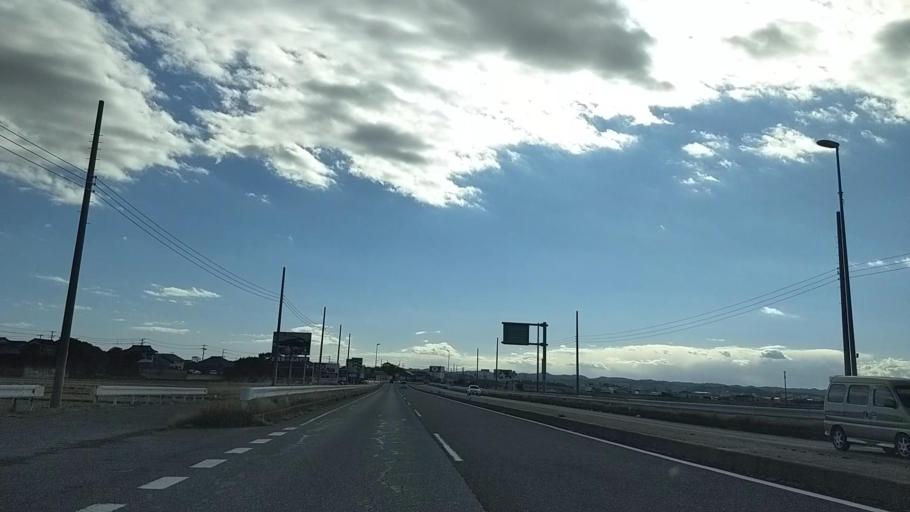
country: JP
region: Chiba
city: Tateyama
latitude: 35.0222
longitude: 139.8682
